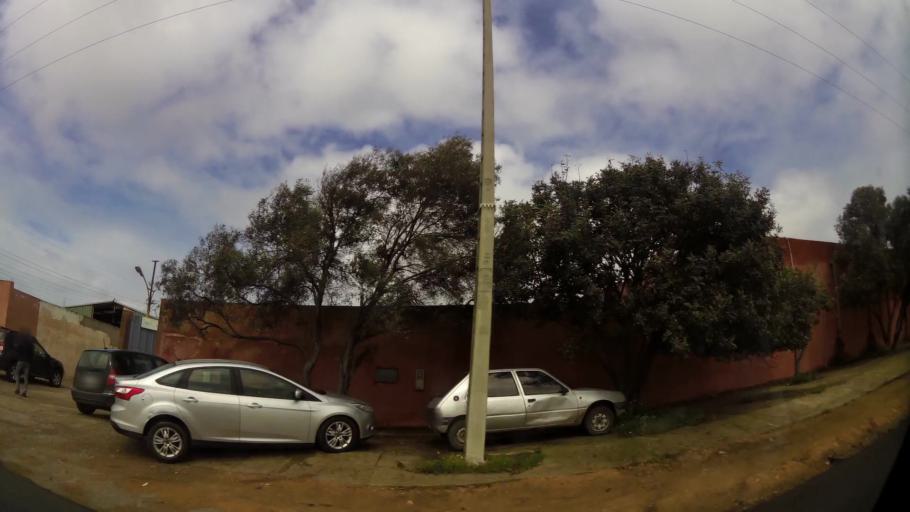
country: MA
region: Grand Casablanca
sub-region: Mohammedia
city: Mohammedia
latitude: 33.6514
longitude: -7.4583
